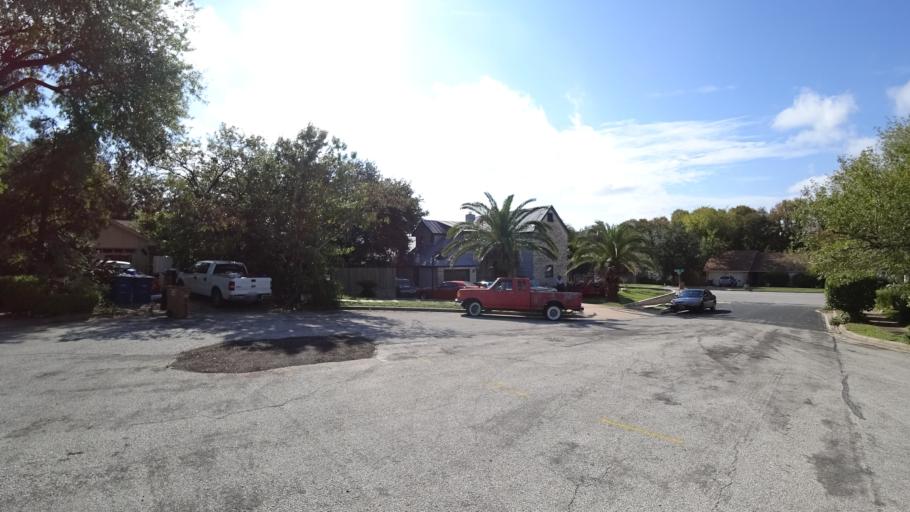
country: US
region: Texas
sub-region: Travis County
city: Shady Hollow
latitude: 30.1955
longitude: -97.8196
